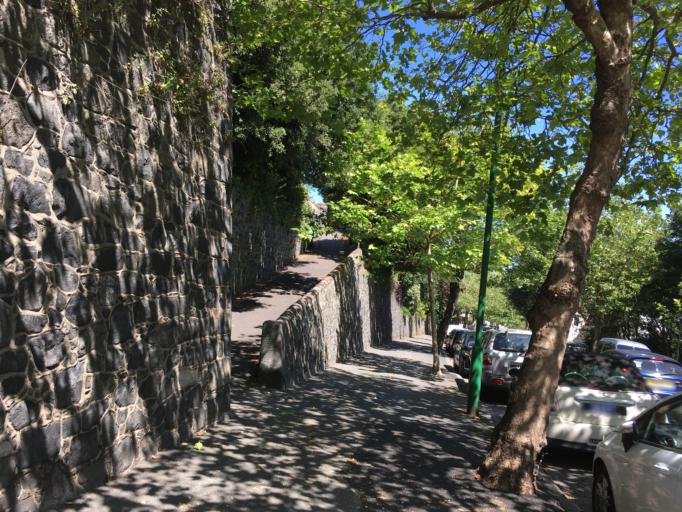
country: GG
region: St Peter Port
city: Saint Peter Port
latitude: 49.4588
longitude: -2.5381
